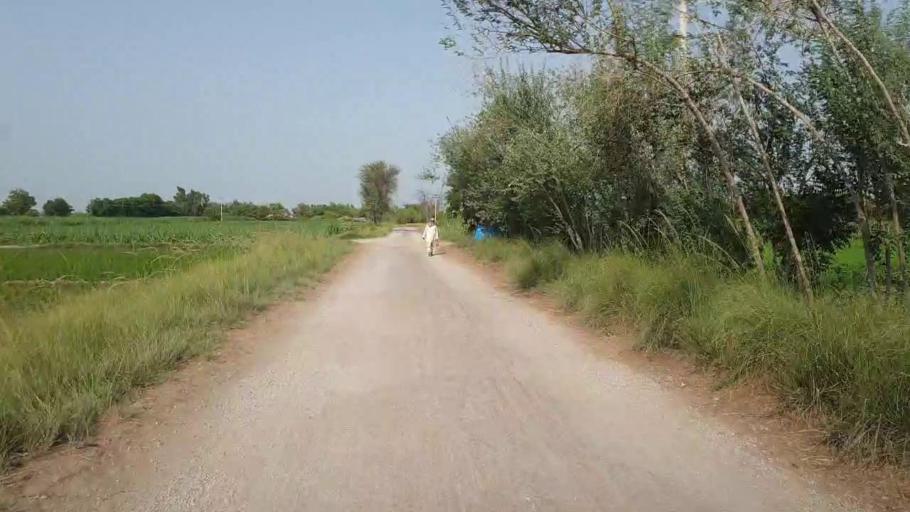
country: PK
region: Sindh
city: Daur
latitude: 26.3226
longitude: 68.1509
